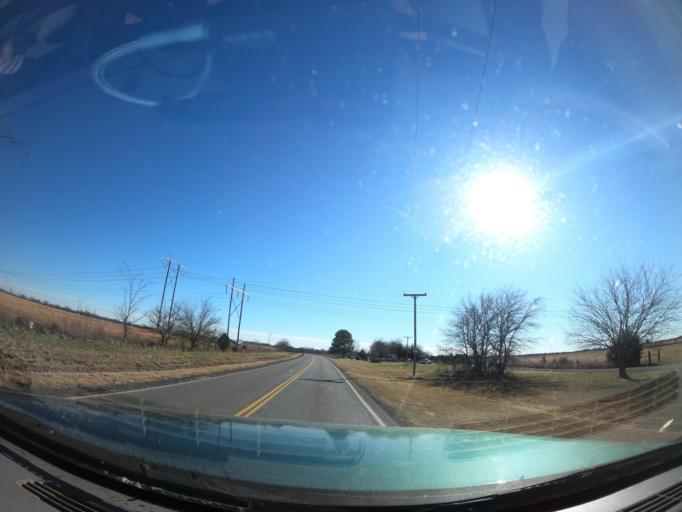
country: US
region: Oklahoma
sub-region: McIntosh County
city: Checotah
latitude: 35.5764
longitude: -95.6596
